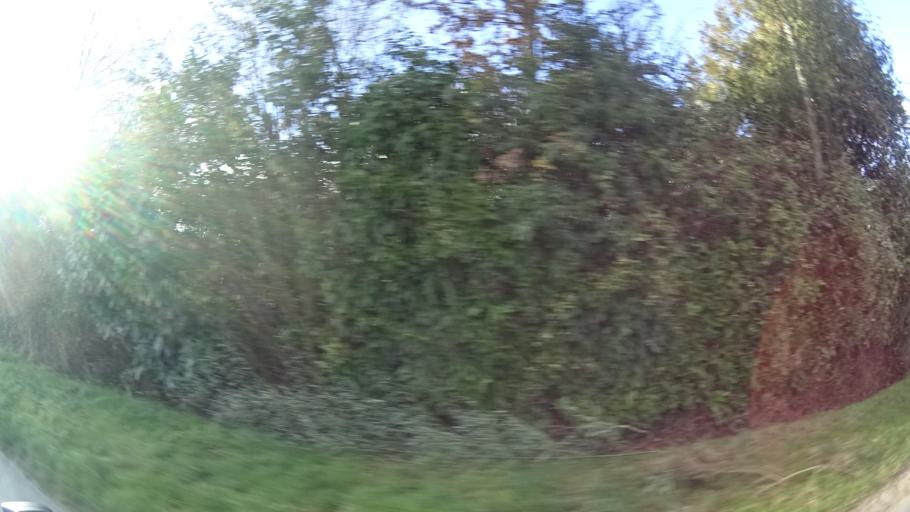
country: FR
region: Pays de la Loire
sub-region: Departement de la Loire-Atlantique
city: Guemene-Penfao
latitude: 47.6085
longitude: -1.8420
